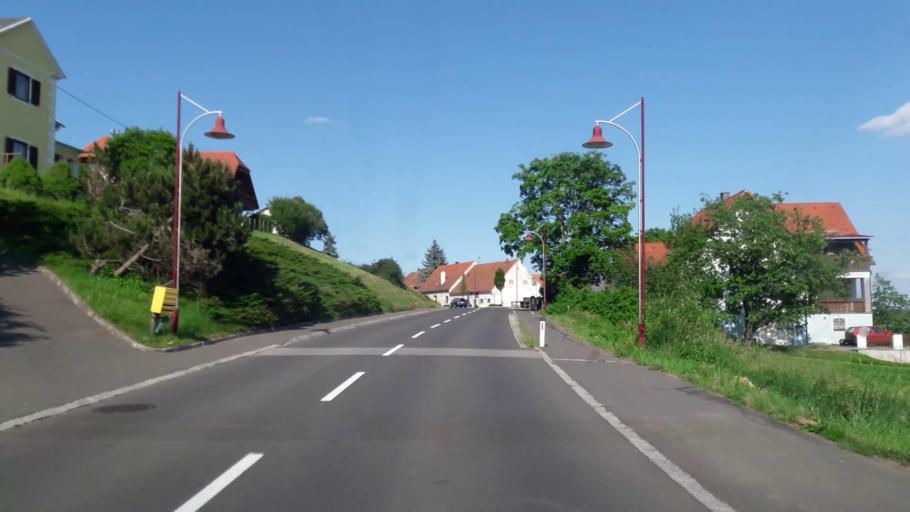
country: AT
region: Styria
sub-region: Politischer Bezirk Suedoststeiermark
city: Fehring
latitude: 46.9528
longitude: 16.0117
